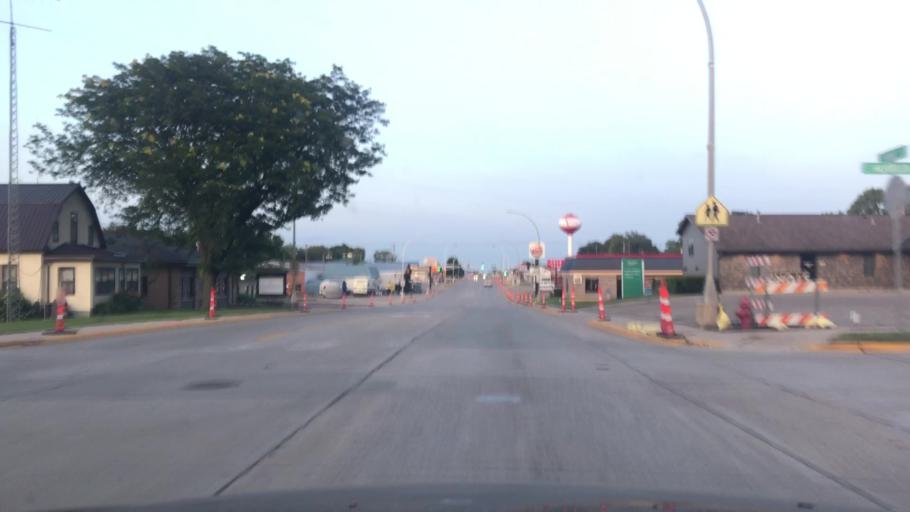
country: US
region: Minnesota
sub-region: Redwood County
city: Redwood Falls
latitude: 44.5414
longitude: -95.1131
